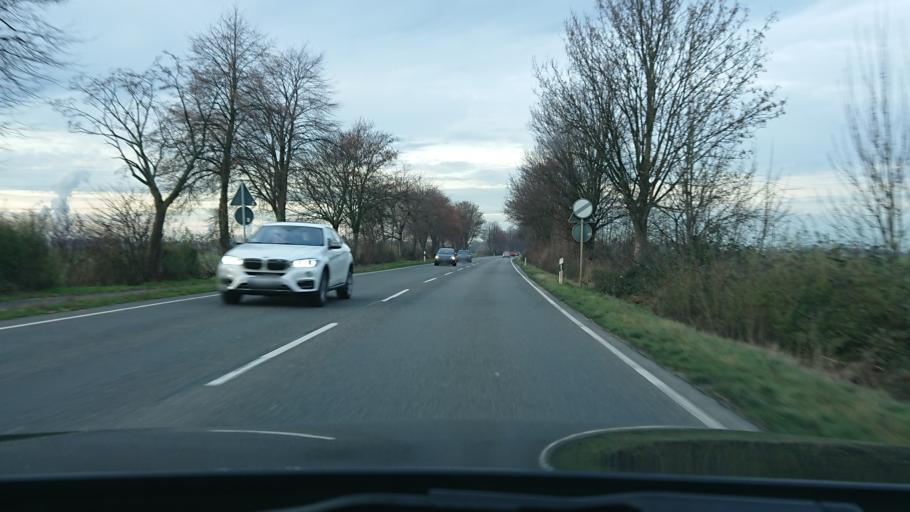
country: DE
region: North Rhine-Westphalia
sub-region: Regierungsbezirk Koln
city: Frechen
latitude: 50.9456
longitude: 6.8075
